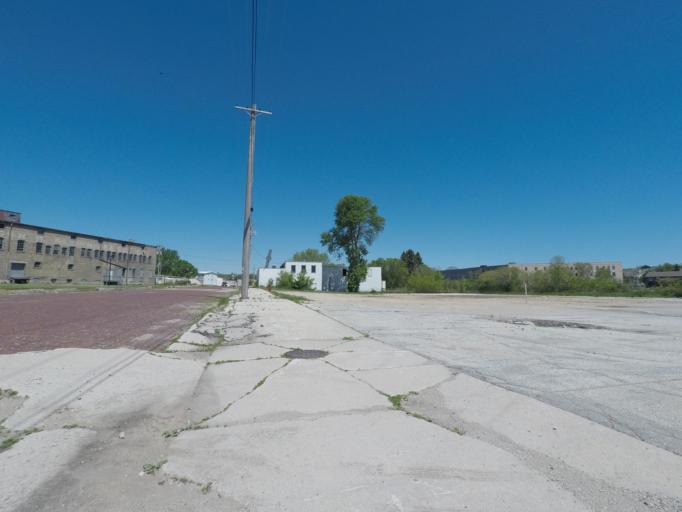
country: US
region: Wisconsin
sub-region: Sheboygan County
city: Sheboygan
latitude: 43.7512
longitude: -87.7197
